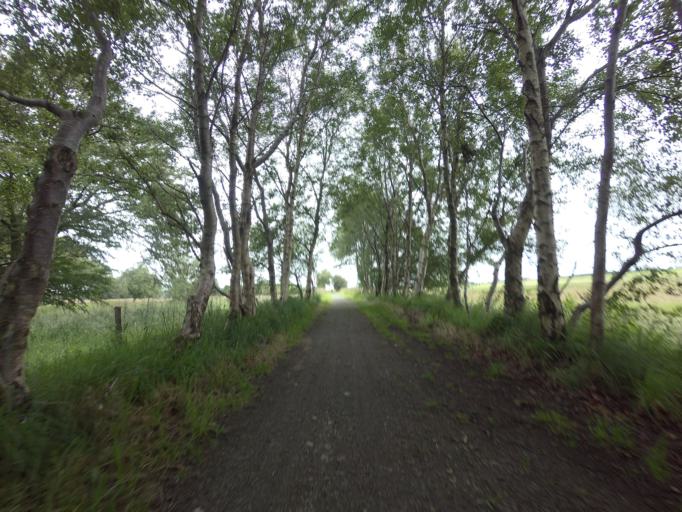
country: GB
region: Scotland
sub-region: Aberdeenshire
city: Mintlaw
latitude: 57.4918
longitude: -2.1353
